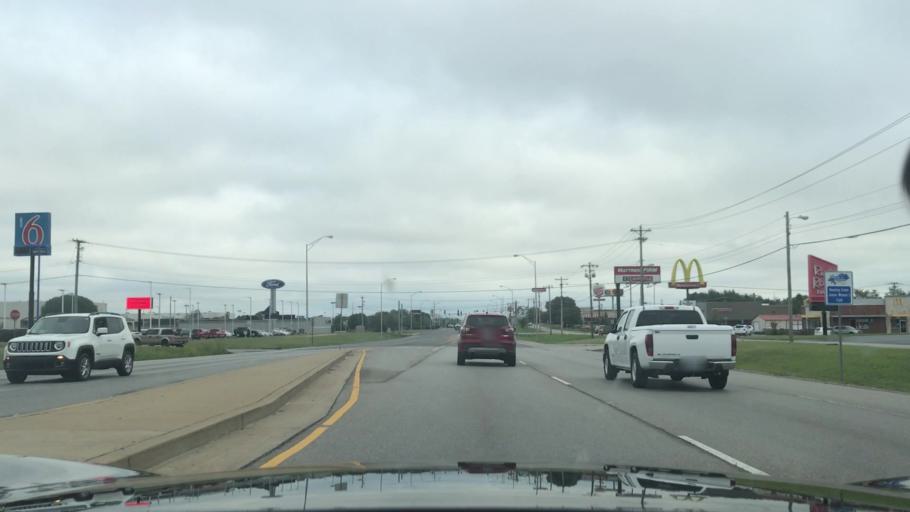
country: US
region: Kentucky
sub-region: Warren County
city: Bowling Green
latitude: 36.9407
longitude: -86.4209
